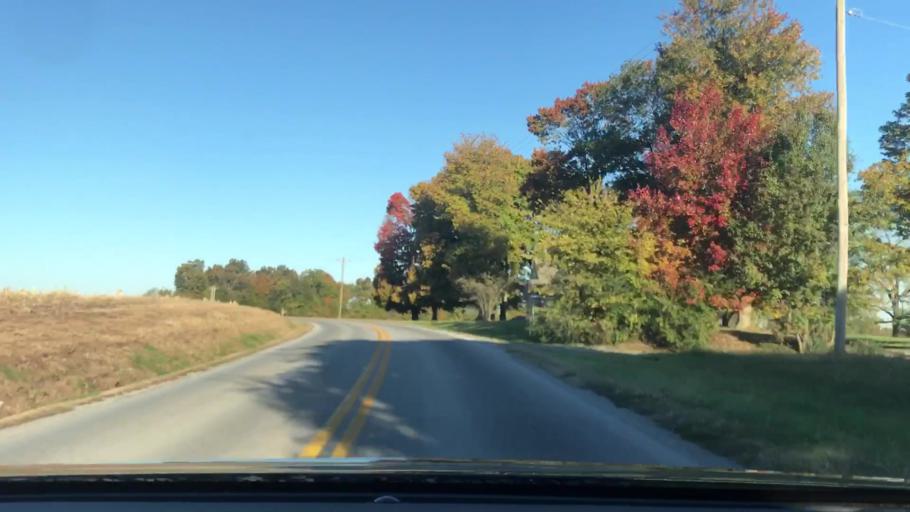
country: US
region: Kentucky
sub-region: Logan County
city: Auburn
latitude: 36.8453
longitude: -86.6979
